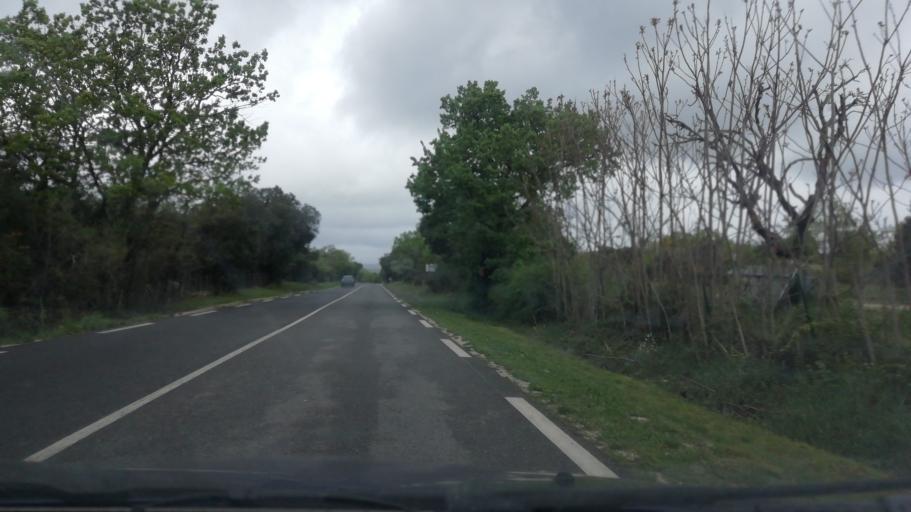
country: FR
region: Languedoc-Roussillon
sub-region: Departement de l'Herault
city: Les Matelles
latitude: 43.7410
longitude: 3.7734
